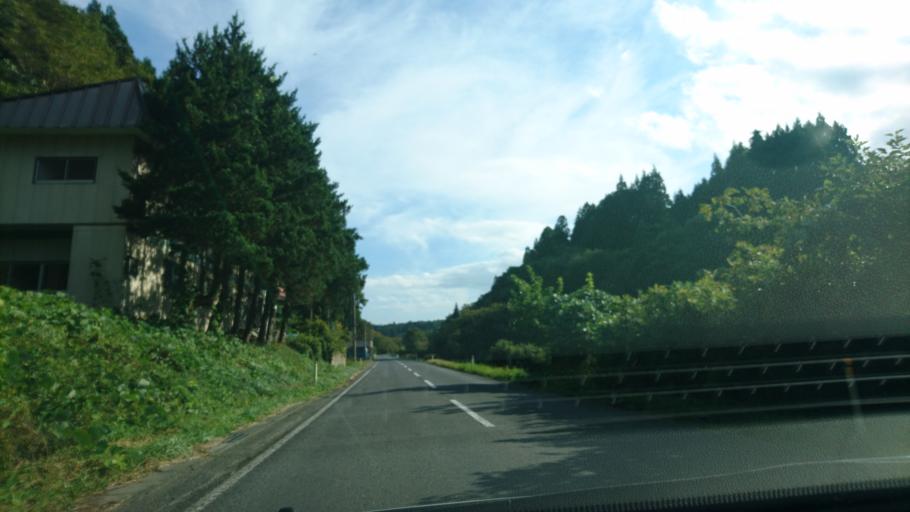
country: JP
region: Iwate
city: Ichinoseki
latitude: 38.8612
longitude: 141.3308
